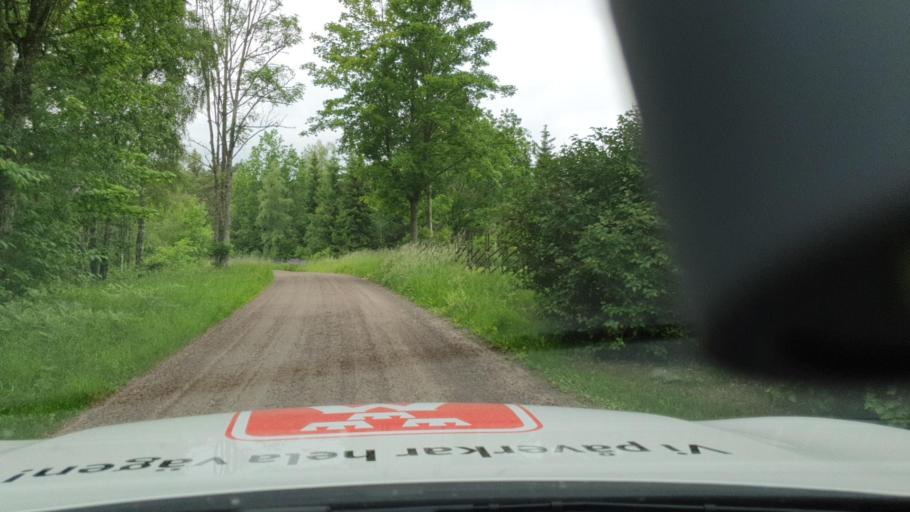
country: SE
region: Vaestra Goetaland
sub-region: Hjo Kommun
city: Hjo
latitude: 58.3469
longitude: 14.3013
